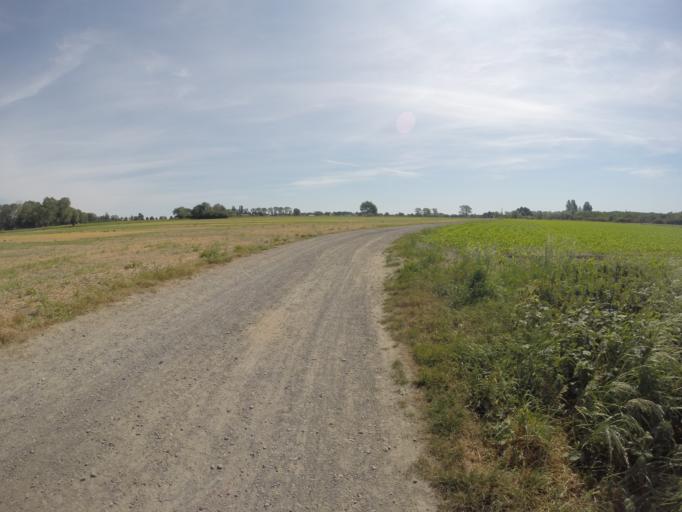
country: BE
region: Flanders
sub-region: Provincie West-Vlaanderen
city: Beernem
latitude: 51.1776
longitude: 3.3270
